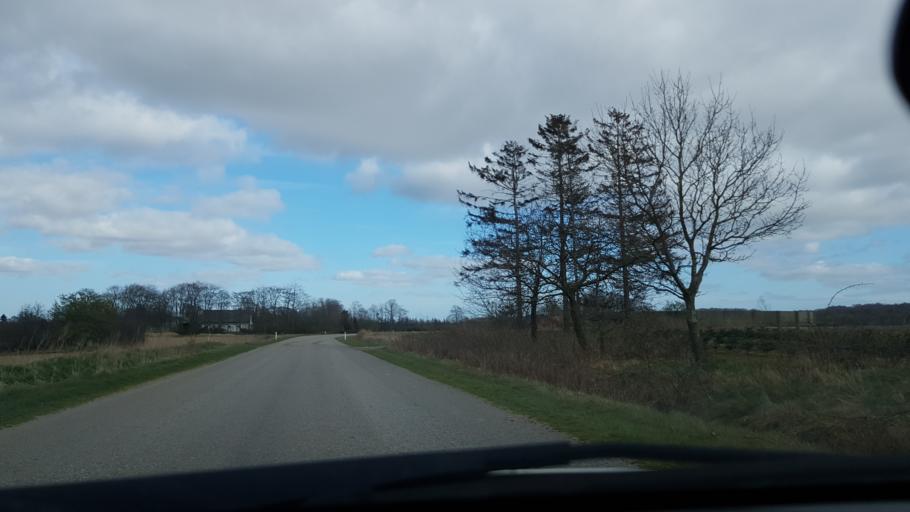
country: DK
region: South Denmark
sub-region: Vejen Kommune
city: Brorup
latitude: 55.4378
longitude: 9.0262
